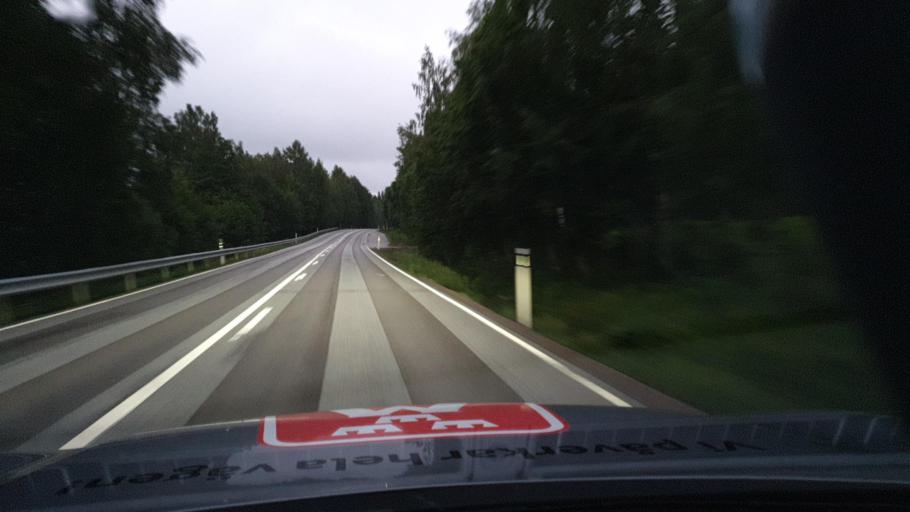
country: SE
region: OErebro
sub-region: Hallefors Kommun
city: Haellefors
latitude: 59.7486
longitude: 14.4452
